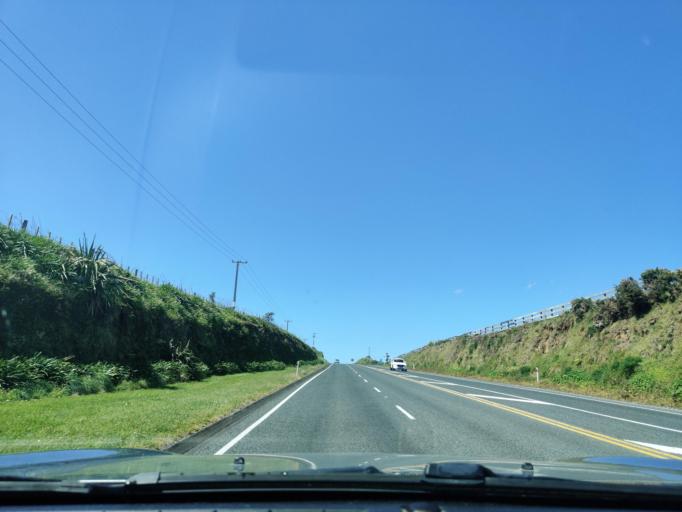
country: NZ
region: Taranaki
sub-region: New Plymouth District
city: New Plymouth
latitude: -39.1042
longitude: 173.9819
